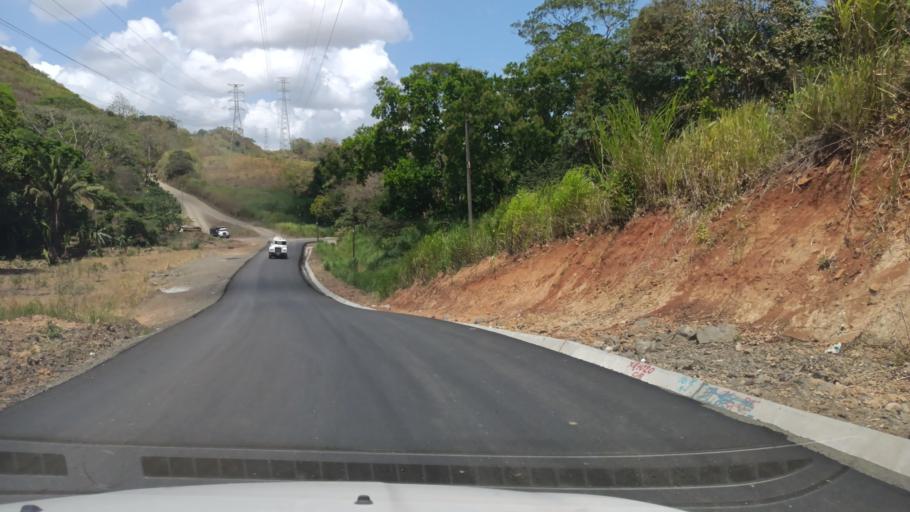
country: PA
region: Panama
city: Alcalde Diaz
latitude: 9.0837
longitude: -79.5782
